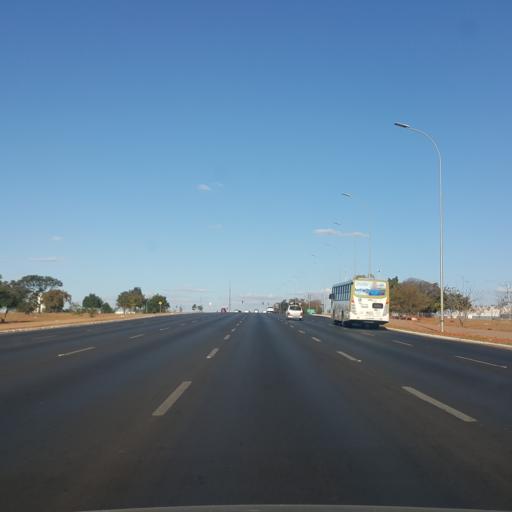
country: BR
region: Federal District
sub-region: Brasilia
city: Brasilia
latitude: -15.7832
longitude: -47.9193
